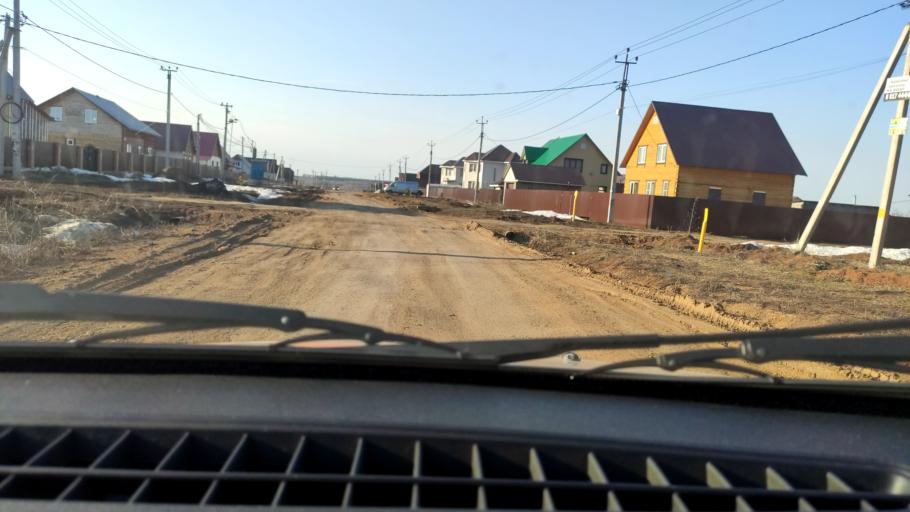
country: RU
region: Bashkortostan
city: Iglino
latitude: 54.8212
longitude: 56.4416
